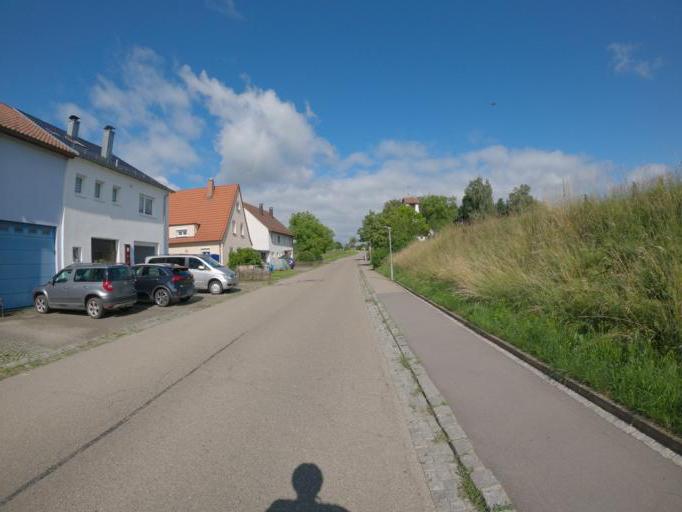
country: DE
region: Baden-Wuerttemberg
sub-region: Regierungsbezirk Stuttgart
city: Ebersbach an der Fils
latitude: 48.7264
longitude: 9.5470
